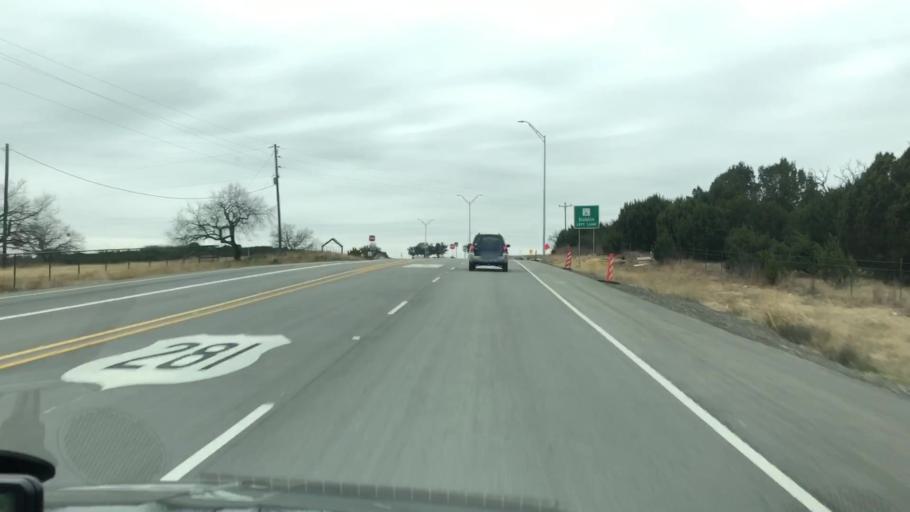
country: US
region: Texas
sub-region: Hamilton County
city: Hico
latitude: 32.0286
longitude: -98.0792
